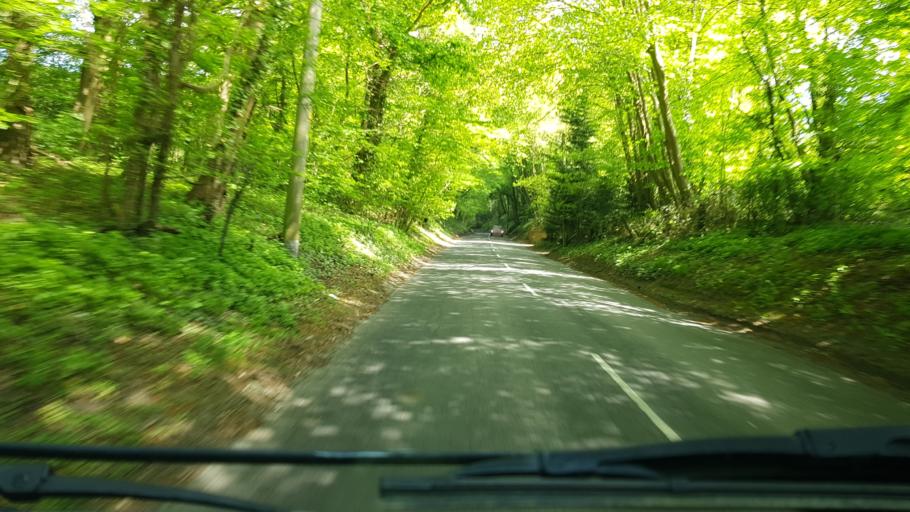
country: GB
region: England
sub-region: East Sussex
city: Robertsbridge
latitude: 51.0311
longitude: 0.4533
